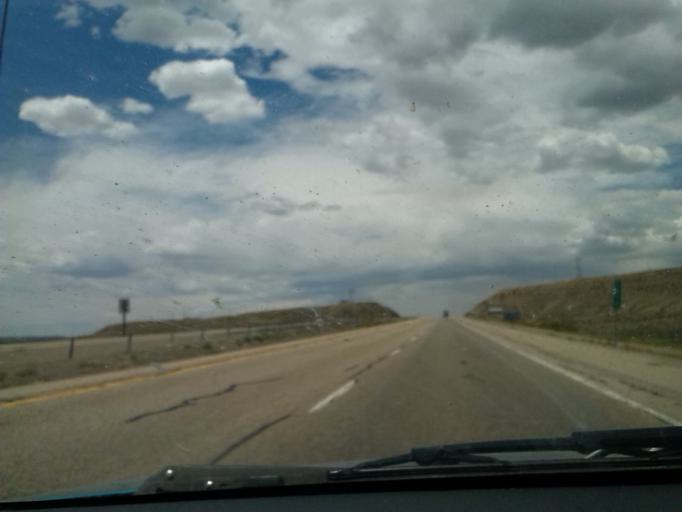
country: US
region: Wyoming
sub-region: Carbon County
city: Rawlins
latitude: 41.7819
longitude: -107.1351
